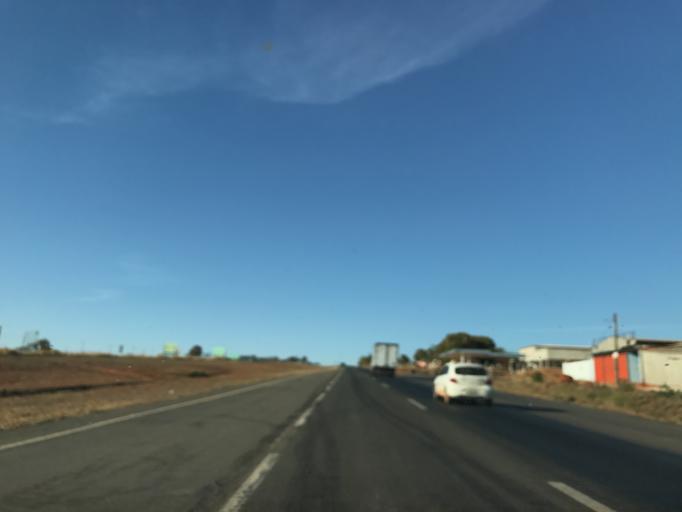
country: BR
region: Goias
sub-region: Aparecida De Goiania
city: Aparecida de Goiania
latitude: -16.8772
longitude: -49.2525
